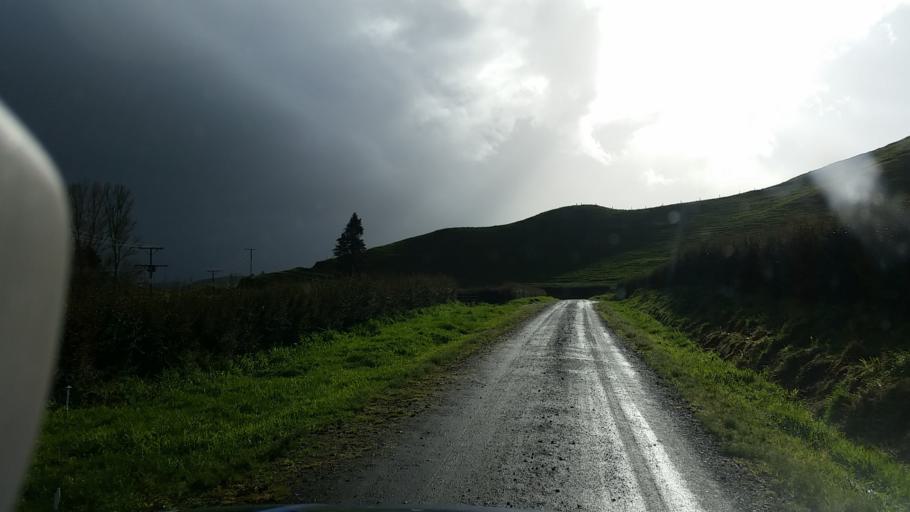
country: NZ
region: Taranaki
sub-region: South Taranaki District
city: Eltham
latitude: -39.3471
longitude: 174.4445
